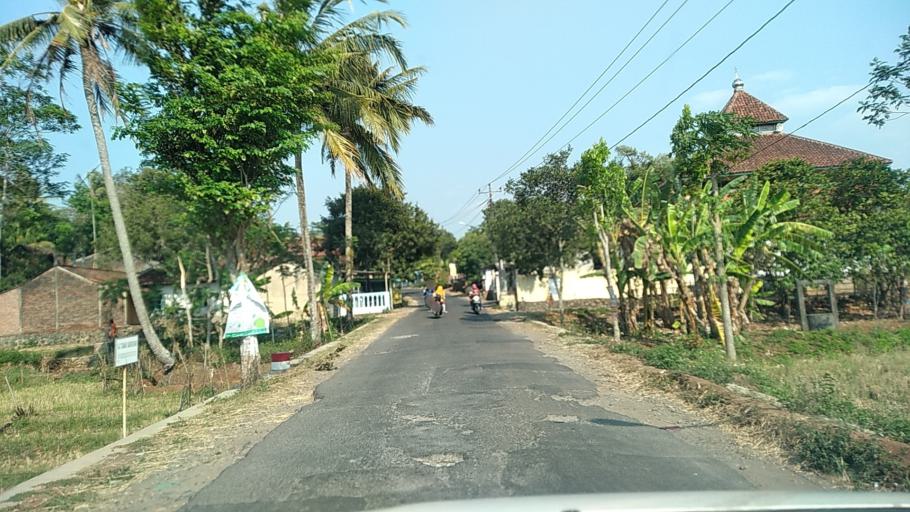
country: ID
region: Central Java
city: Semarang
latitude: -7.0533
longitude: 110.3309
